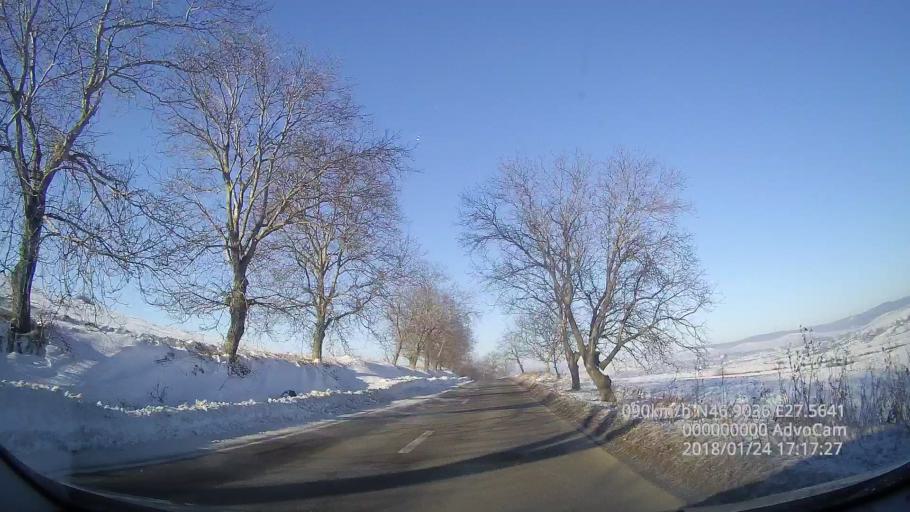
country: RO
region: Iasi
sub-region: Comuna Scanteia
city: Scanteia
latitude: 46.9042
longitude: 27.5642
